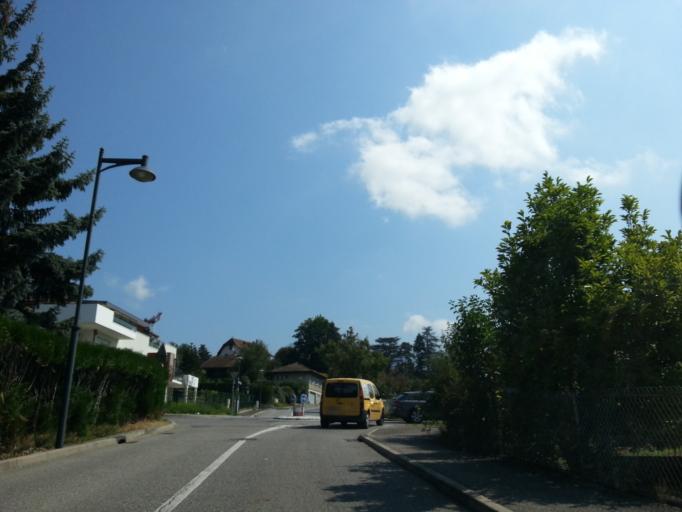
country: FR
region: Rhone-Alpes
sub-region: Departement de la Haute-Savoie
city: Annecy-le-Vieux
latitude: 45.9169
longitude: 6.1510
